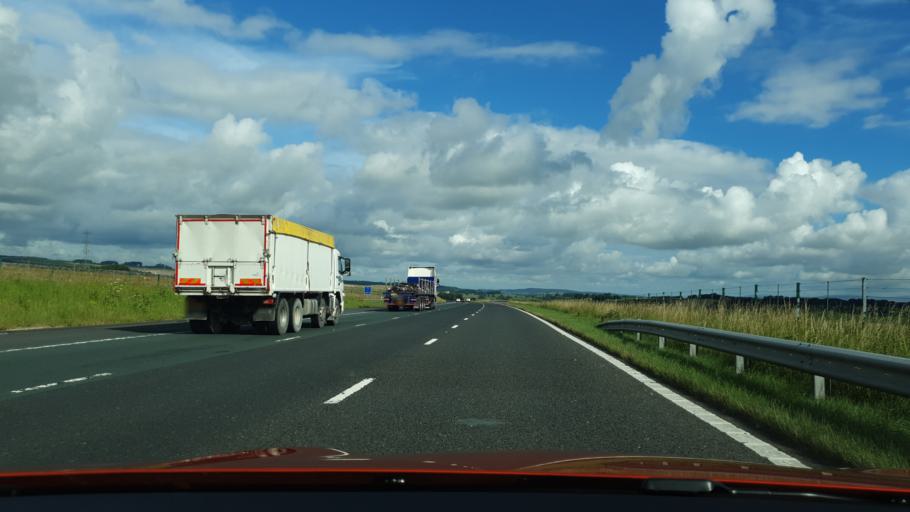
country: GB
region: England
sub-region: Cumbria
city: Penrith
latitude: 54.5389
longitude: -2.6626
